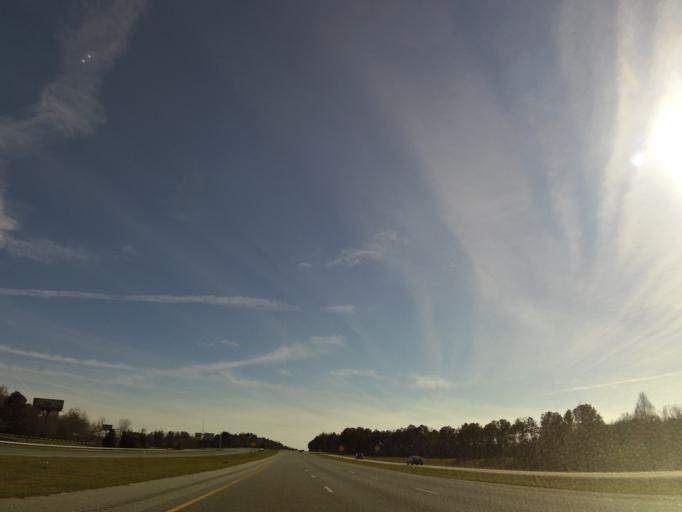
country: US
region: Alabama
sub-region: Russell County
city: Phenix City
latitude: 32.5432
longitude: -84.9608
